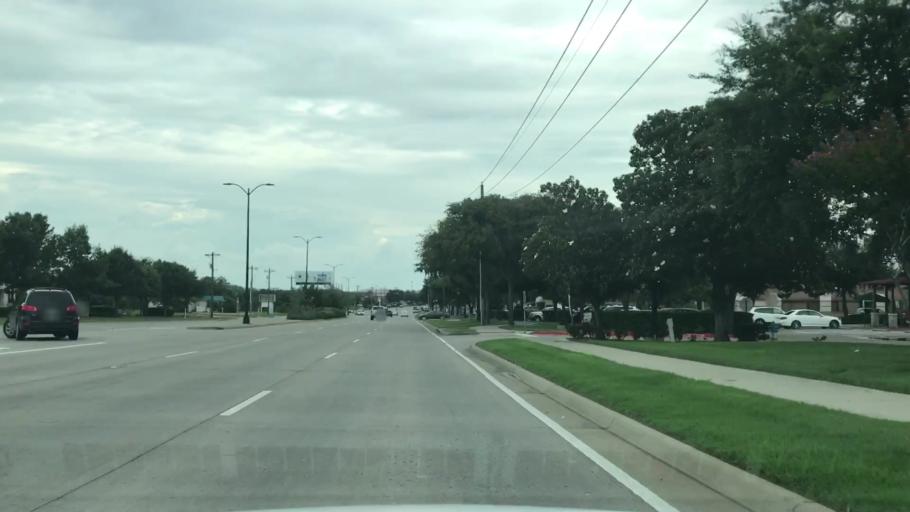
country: US
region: Texas
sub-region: Collin County
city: Frisco
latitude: 33.1378
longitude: -96.8045
